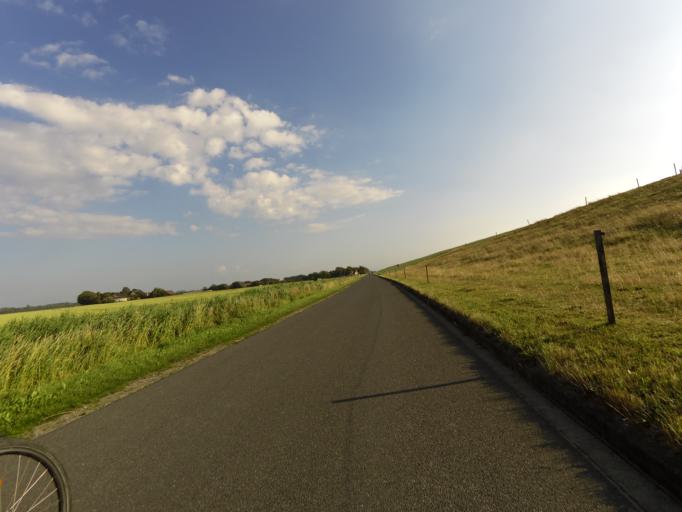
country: DE
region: Lower Saxony
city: Nordholz
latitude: 53.7817
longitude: 8.5500
